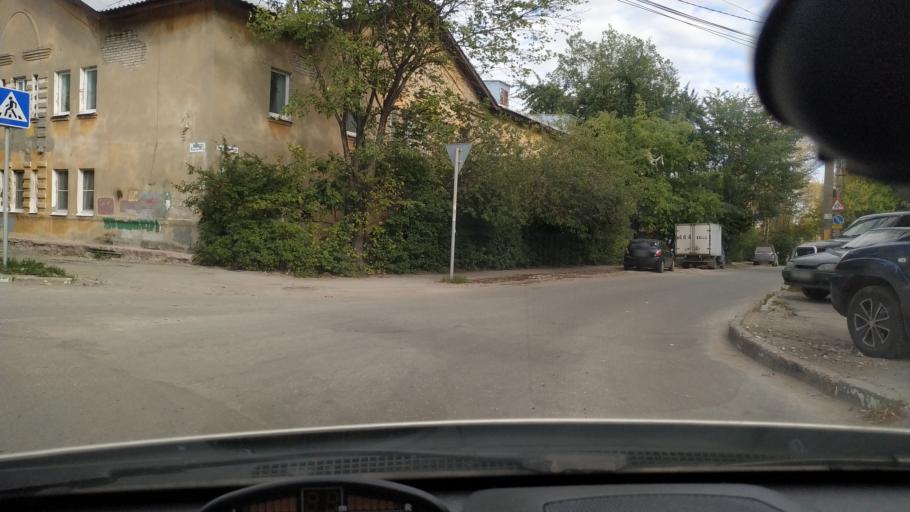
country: RU
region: Rjazan
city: Ryazan'
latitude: 54.6055
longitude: 39.7194
